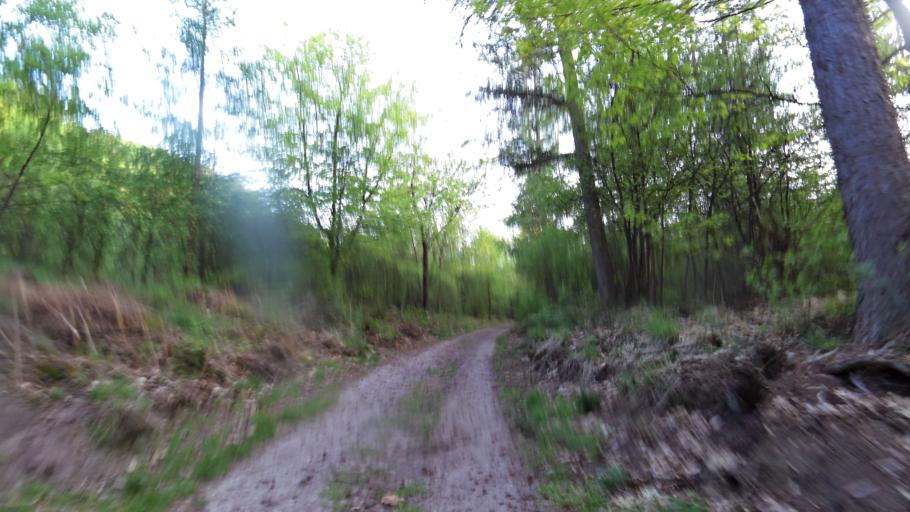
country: NL
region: Gelderland
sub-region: Gemeente Ede
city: Ede
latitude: 52.0598
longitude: 5.6772
